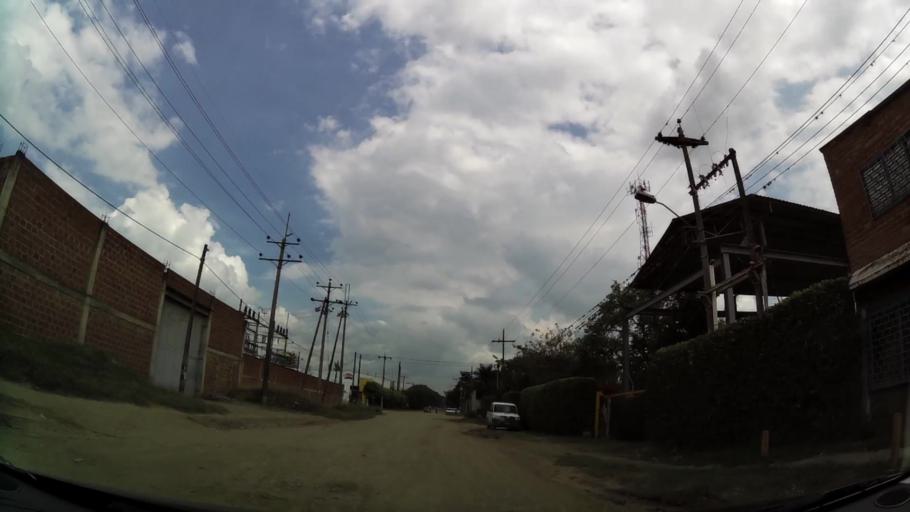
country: CO
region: Valle del Cauca
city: Cali
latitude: 3.4960
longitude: -76.4731
